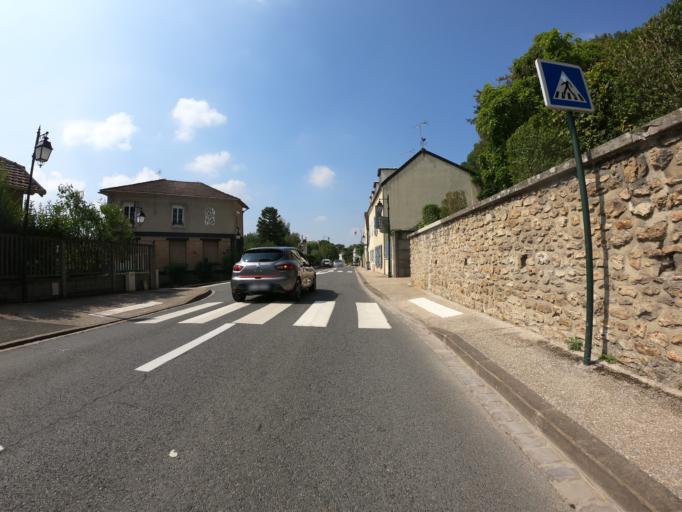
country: FR
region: Ile-de-France
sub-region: Departement de l'Essonne
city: Bievres
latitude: 48.7610
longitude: 2.2222
